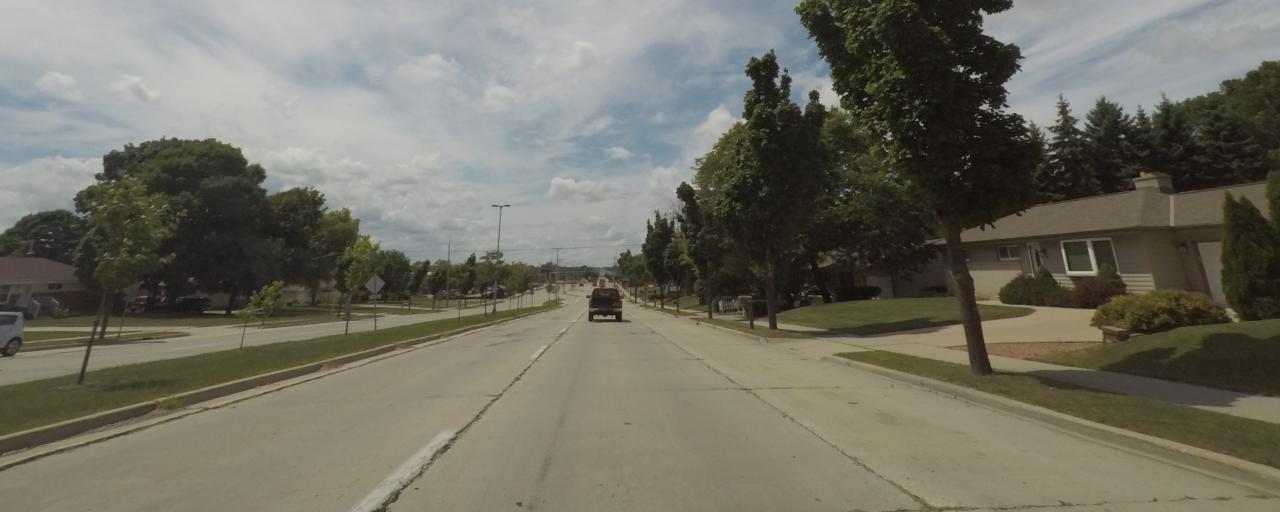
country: US
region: Wisconsin
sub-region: Milwaukee County
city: Greenfield
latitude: 42.9594
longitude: -88.0039
